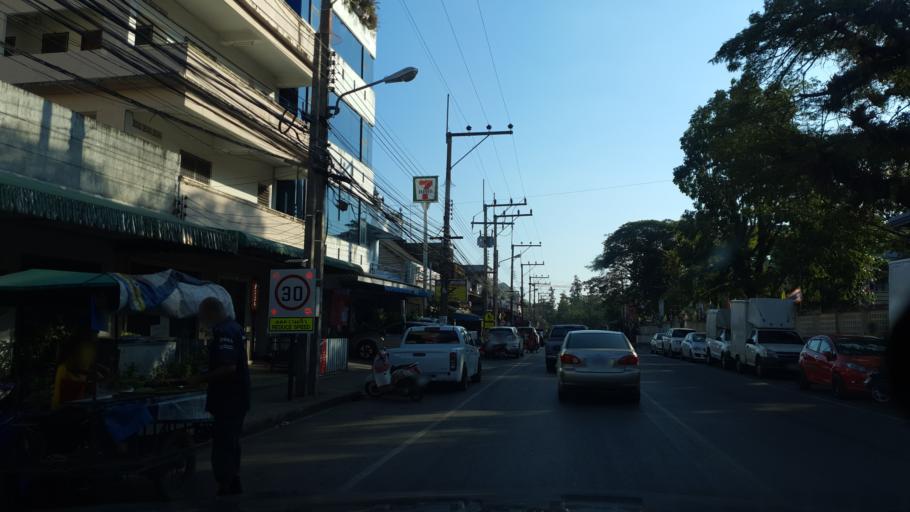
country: TH
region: Krabi
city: Krabi
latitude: 8.1014
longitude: 98.9113
